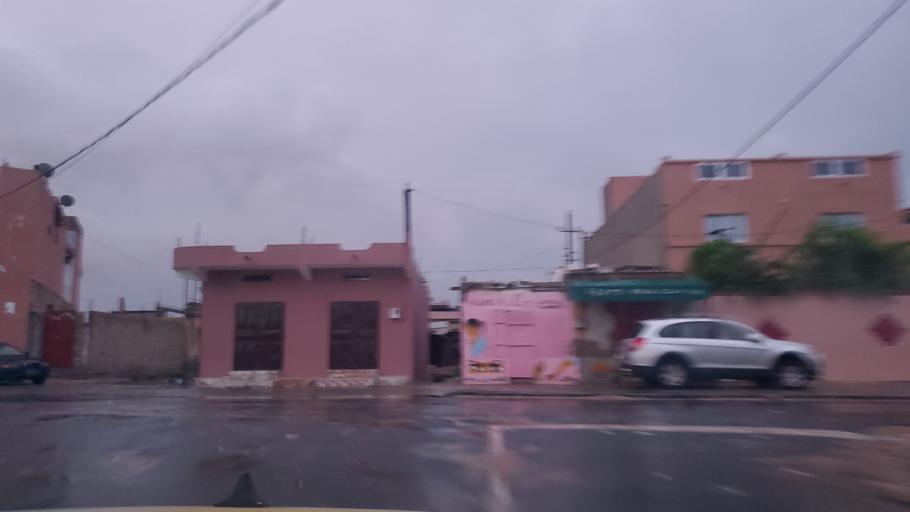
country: SN
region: Saint-Louis
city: Saint-Louis
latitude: 16.0110
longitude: -16.4935
